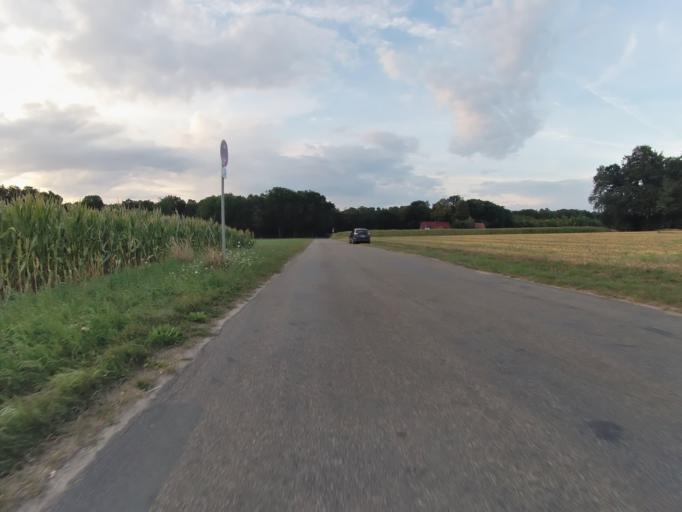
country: DE
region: North Rhine-Westphalia
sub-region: Regierungsbezirk Munster
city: Westerkappeln
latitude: 52.3286
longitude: 7.9100
